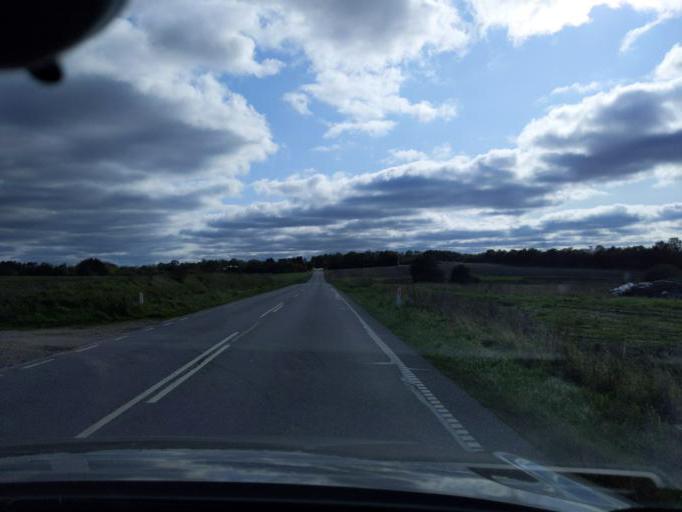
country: DK
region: North Denmark
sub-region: Mariagerfjord Kommune
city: Hobro
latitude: 56.5356
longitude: 9.7257
